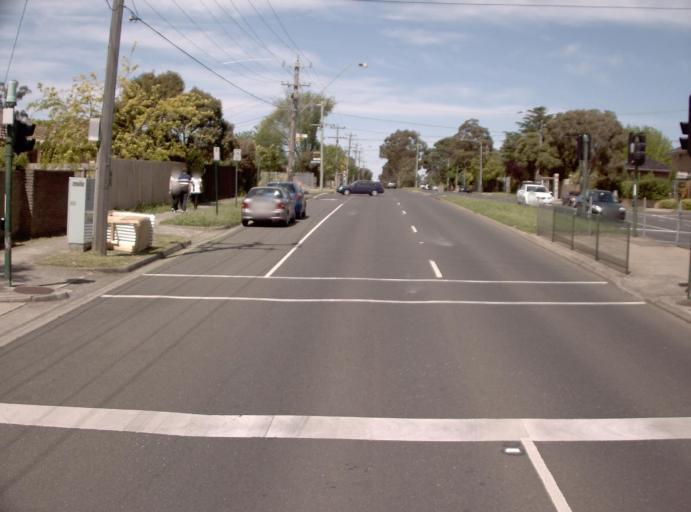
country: AU
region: Victoria
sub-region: Whitehorse
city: Blackburn South
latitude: -37.8401
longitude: 145.1556
